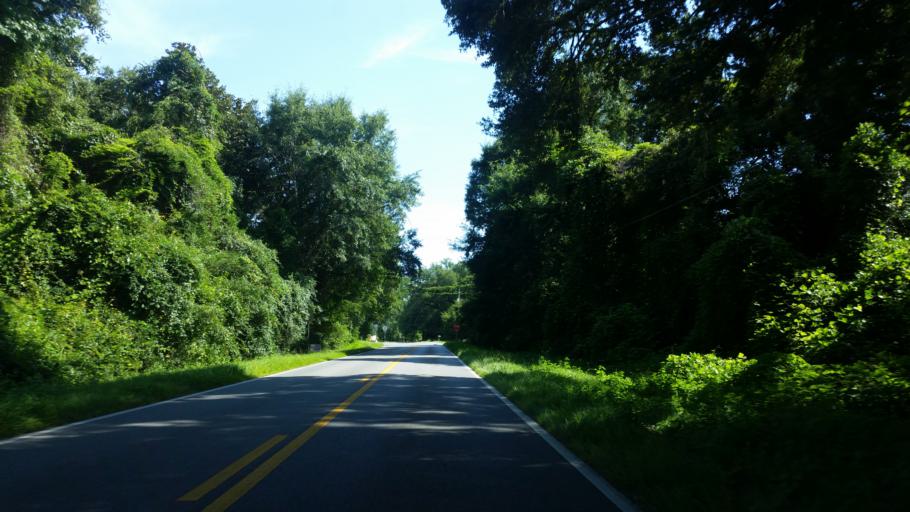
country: US
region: Florida
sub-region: Santa Rosa County
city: Pace
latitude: 30.5910
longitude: -87.1616
